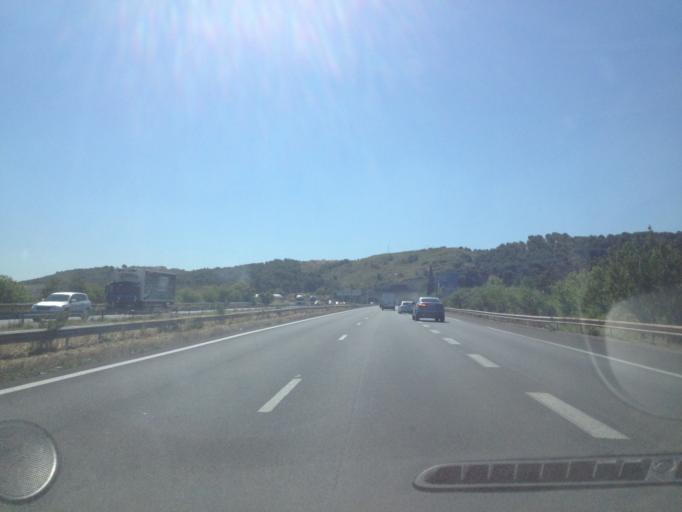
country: FR
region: Provence-Alpes-Cote d'Azur
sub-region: Departement des Bouches-du-Rhone
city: Les Pennes-Mirabeau
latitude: 43.4156
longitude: 5.2773
